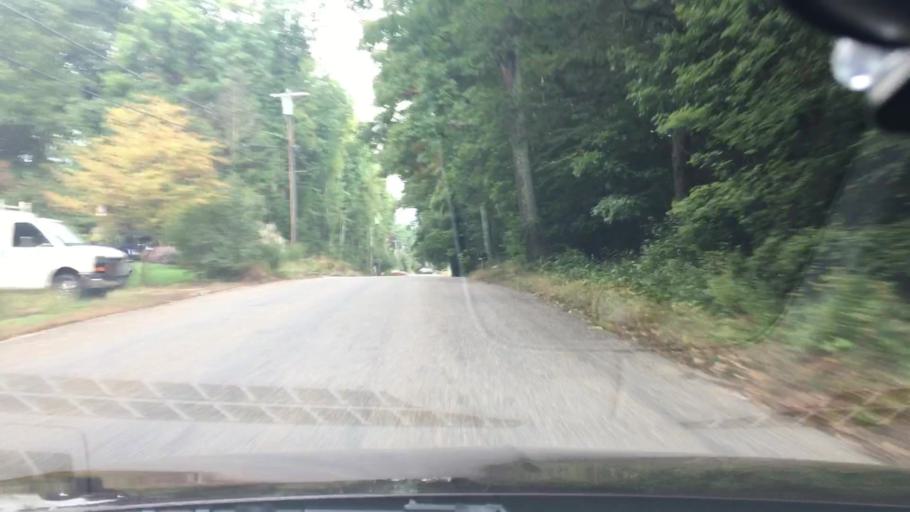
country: US
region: Connecticut
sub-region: Tolland County
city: Stafford
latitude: 41.9907
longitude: -72.3101
